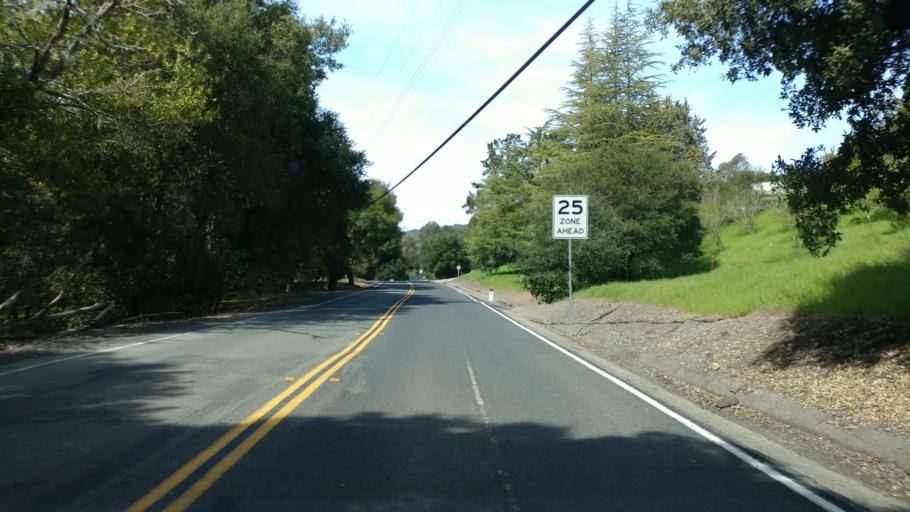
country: US
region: California
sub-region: Contra Costa County
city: Danville
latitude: 37.8051
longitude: -122.0352
